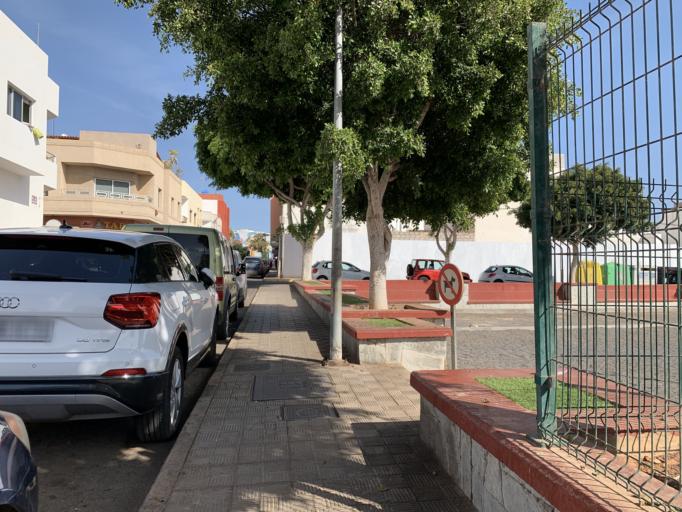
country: ES
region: Canary Islands
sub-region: Provincia de Las Palmas
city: Puerto del Rosario
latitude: 28.4996
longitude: -13.8673
